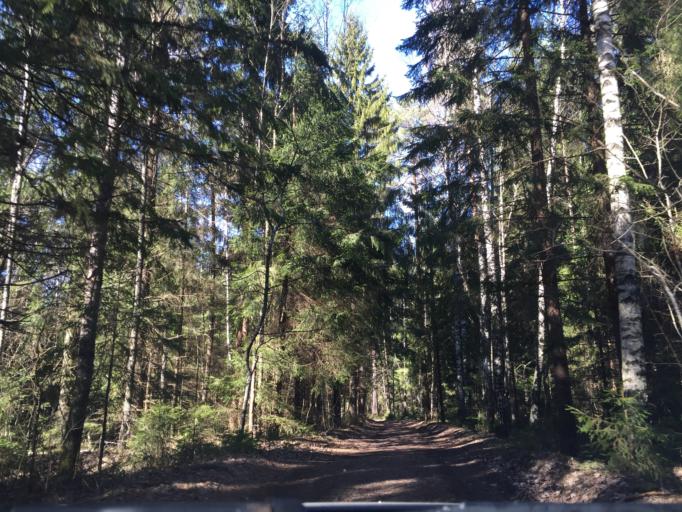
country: LV
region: Incukalns
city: Vangazi
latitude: 57.0943
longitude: 24.5308
